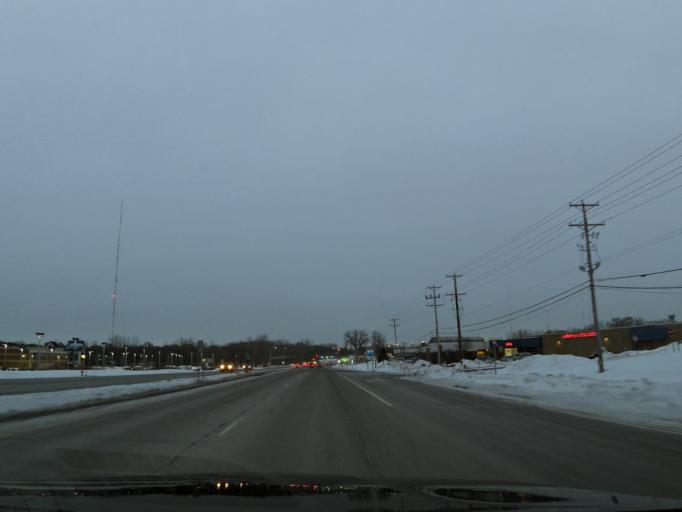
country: US
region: Minnesota
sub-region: Ramsey County
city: Vadnais Heights
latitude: 45.0312
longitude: -93.0456
